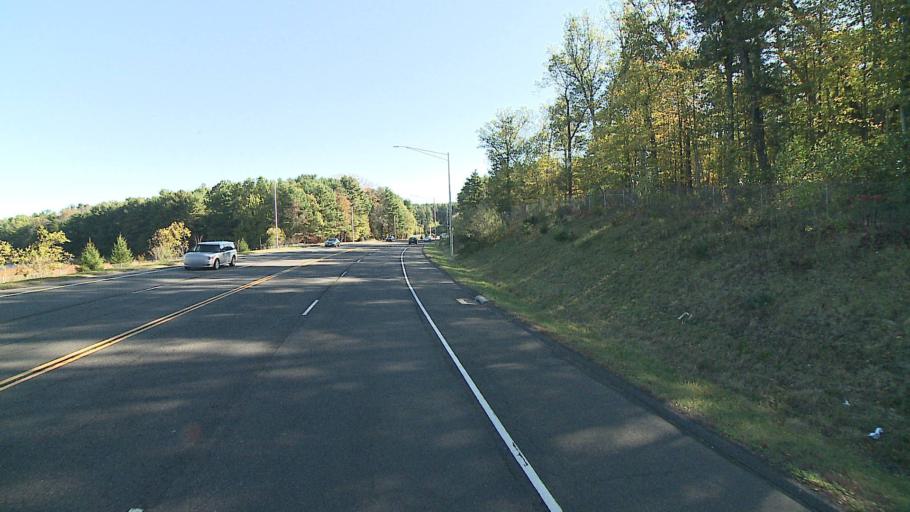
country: US
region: Connecticut
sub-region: Middlesex County
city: Durham
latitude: 41.5379
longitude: -72.7258
